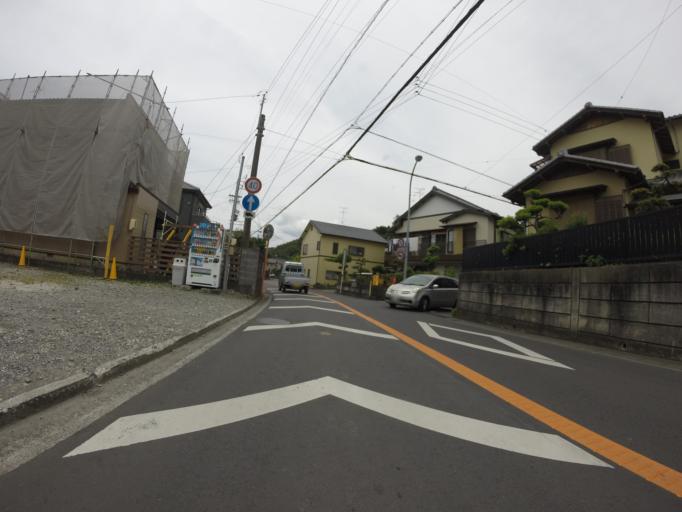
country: JP
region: Shizuoka
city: Shizuoka-shi
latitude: 35.0173
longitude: 138.4158
